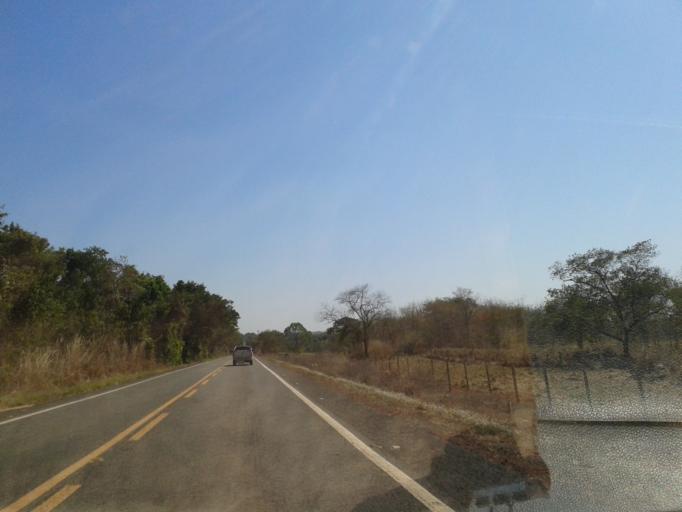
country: BR
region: Goias
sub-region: Sao Miguel Do Araguaia
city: Sao Miguel do Araguaia
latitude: -13.8887
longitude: -50.3289
